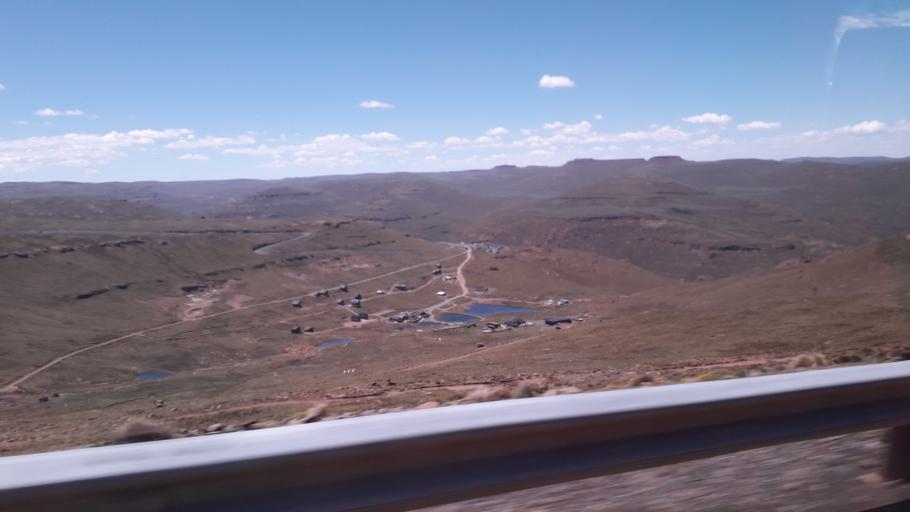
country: ZA
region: Orange Free State
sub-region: Thabo Mofutsanyana District Municipality
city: Phuthaditjhaba
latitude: -28.8136
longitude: 28.7219
